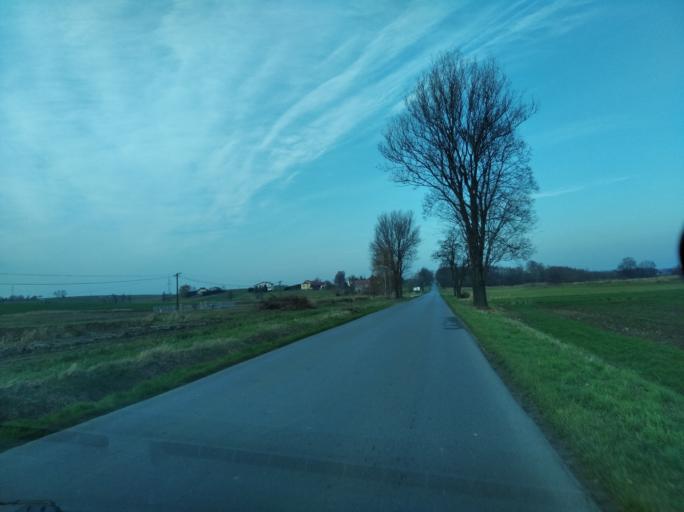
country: PL
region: Subcarpathian Voivodeship
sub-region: Powiat ropczycko-sedziszowski
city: Iwierzyce
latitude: 50.0417
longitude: 21.7457
